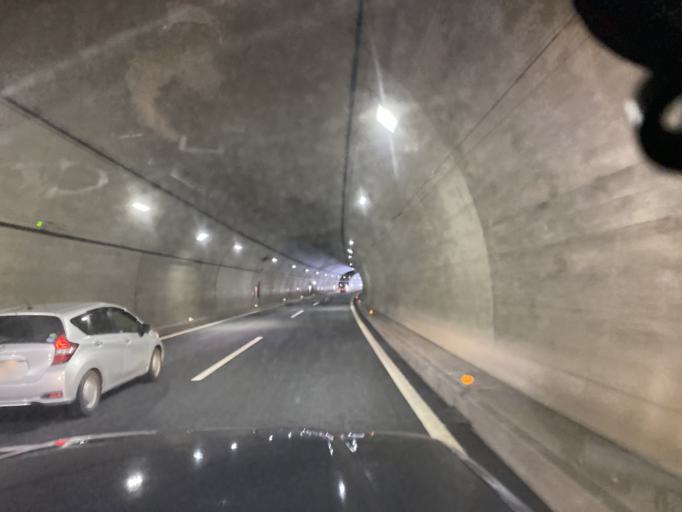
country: JP
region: Gifu
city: Gujo
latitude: 35.9689
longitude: 136.8967
